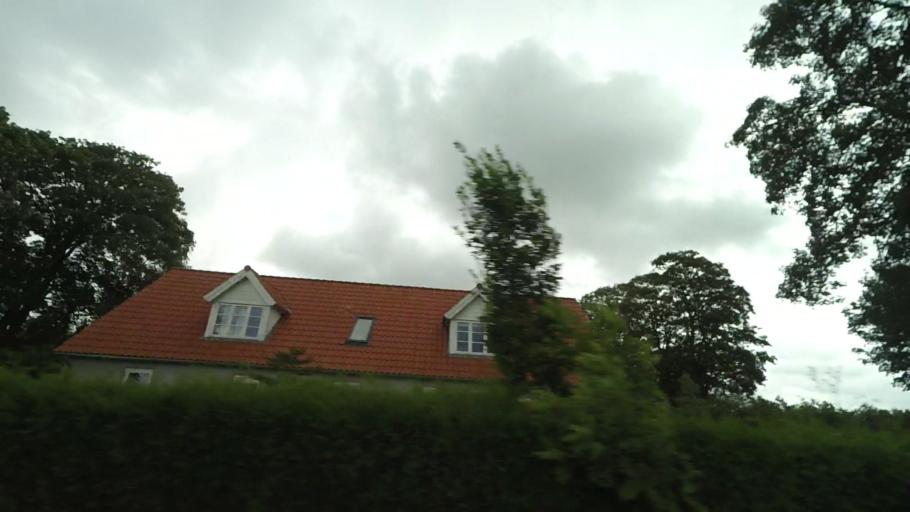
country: DK
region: Central Jutland
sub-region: Syddjurs Kommune
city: Ryomgard
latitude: 56.3898
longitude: 10.5658
